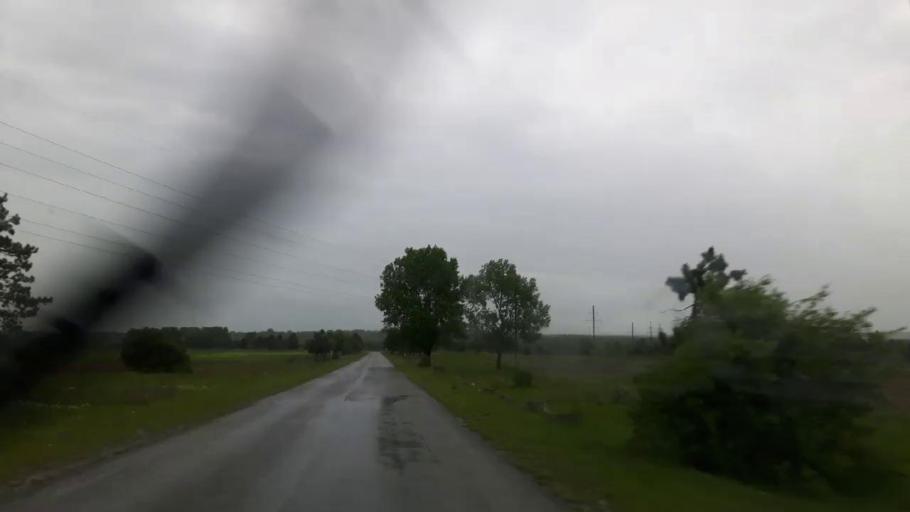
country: GE
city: Agara
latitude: 42.0179
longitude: 43.9087
